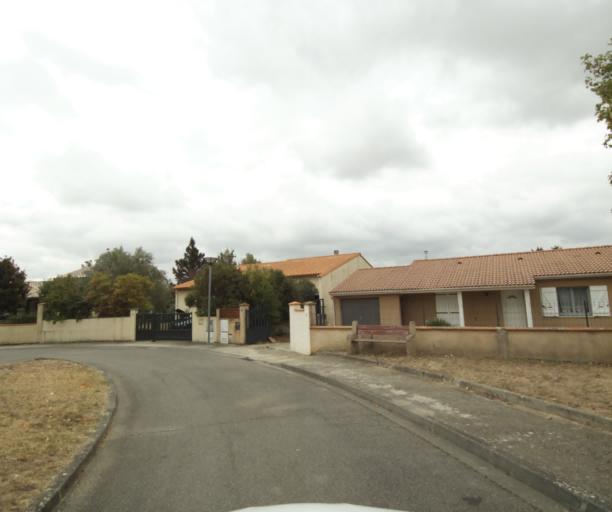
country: FR
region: Midi-Pyrenees
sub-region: Departement de la Haute-Garonne
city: Villefranche-de-Lauragais
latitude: 43.4088
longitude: 1.7151
